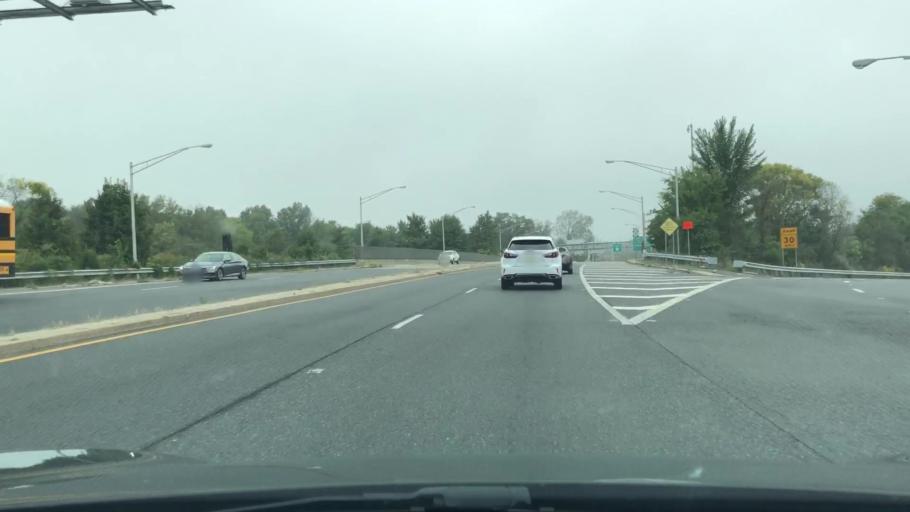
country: US
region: New Jersey
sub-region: Mercer County
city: Ewing
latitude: 40.2894
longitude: -74.7849
